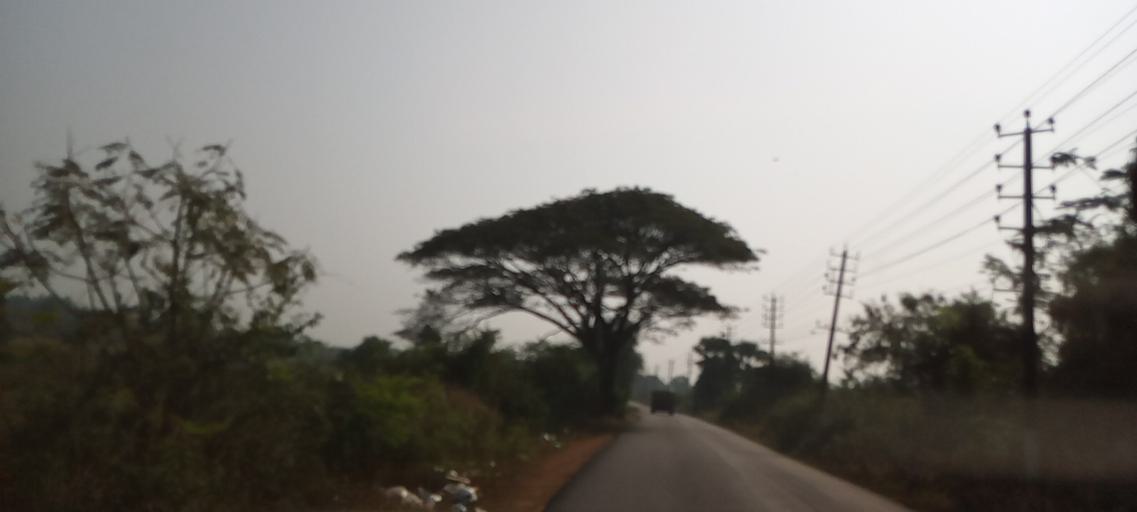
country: IN
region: Karnataka
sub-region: Udupi
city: Coondapoor
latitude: 13.5087
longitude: 74.7135
